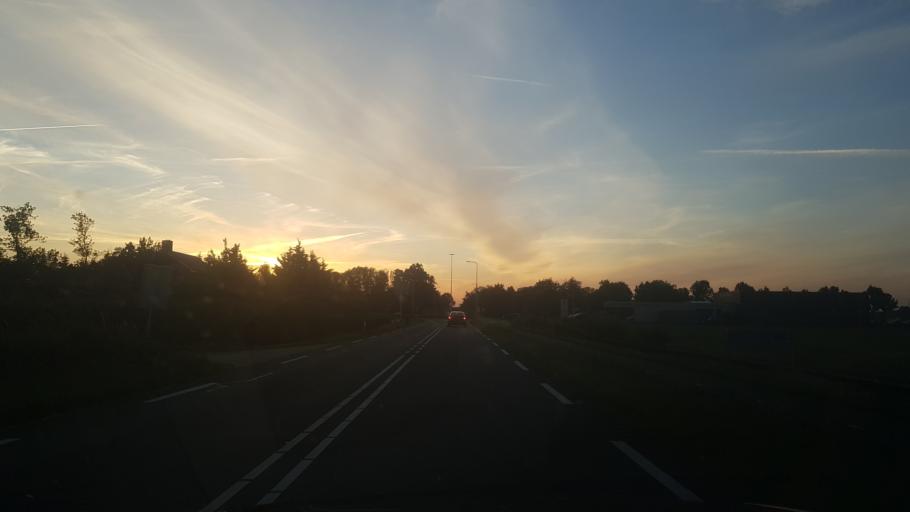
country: NL
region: Flevoland
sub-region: Gemeente Noordoostpolder
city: Emmeloord
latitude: 52.6846
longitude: 5.7405
